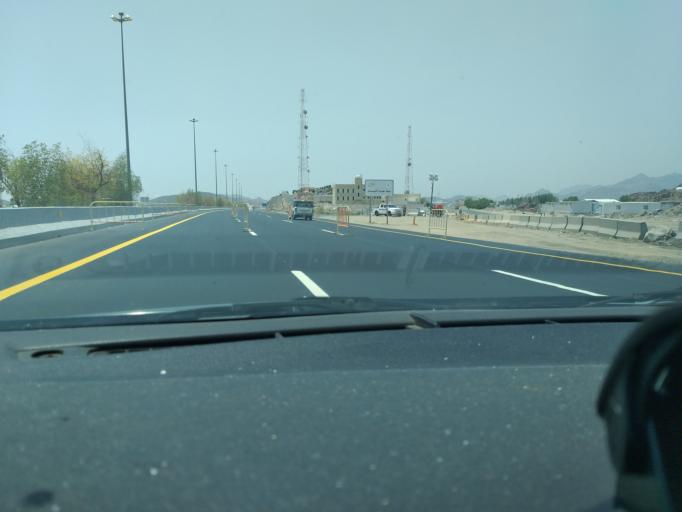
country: SA
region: Makkah
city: Mecca
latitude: 21.3281
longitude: 40.0058
